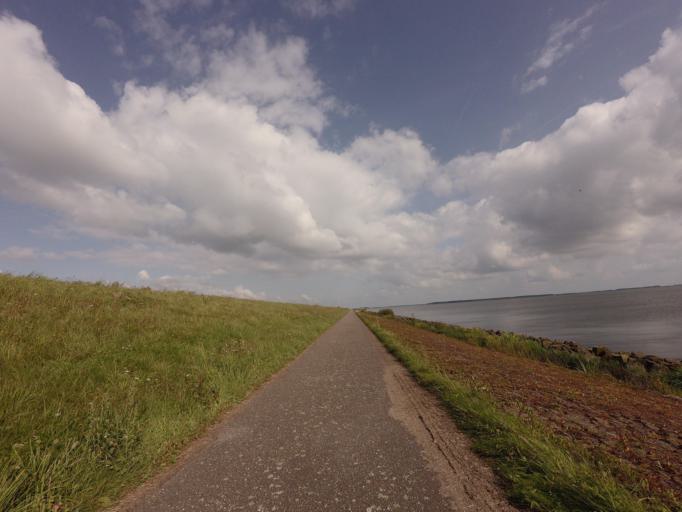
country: NL
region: Flevoland
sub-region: Gemeente Dronten
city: Dronten
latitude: 52.6131
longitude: 5.6944
